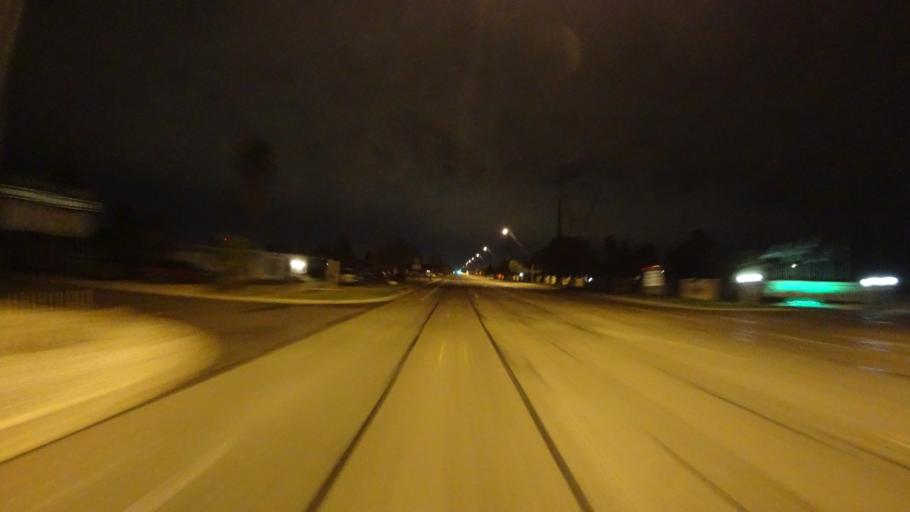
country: US
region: Arizona
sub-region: Pinal County
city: Apache Junction
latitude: 33.4223
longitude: -111.6435
